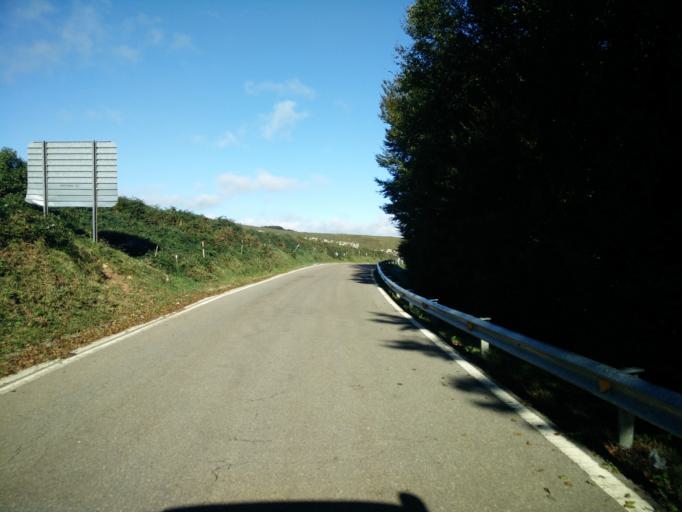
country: ES
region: Cantabria
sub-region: Provincia de Cantabria
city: San Pedro del Romeral
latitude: 43.0413
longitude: -3.8574
